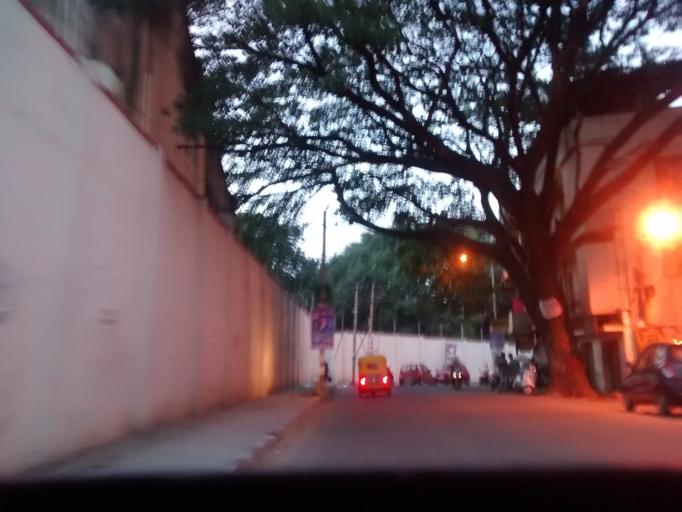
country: IN
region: Karnataka
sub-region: Bangalore Urban
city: Bangalore
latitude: 12.9725
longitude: 77.6616
